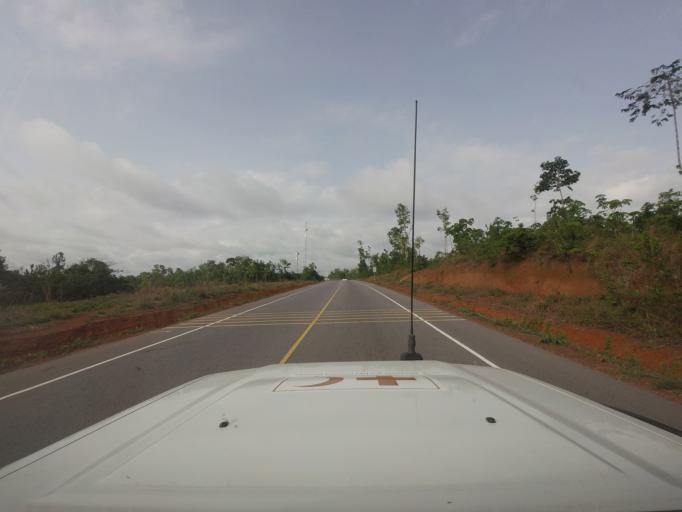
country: LR
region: Bong
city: Gbarnga
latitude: 7.0084
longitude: -9.2832
